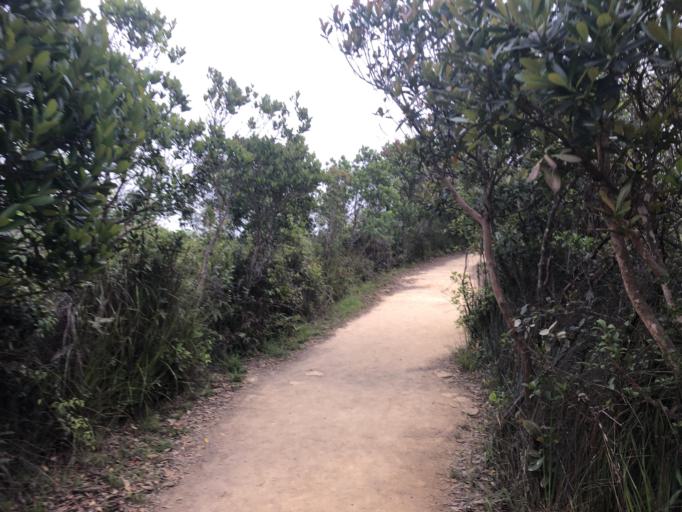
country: HK
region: Sha Tin
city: Sha Tin
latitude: 22.3819
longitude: 114.1537
